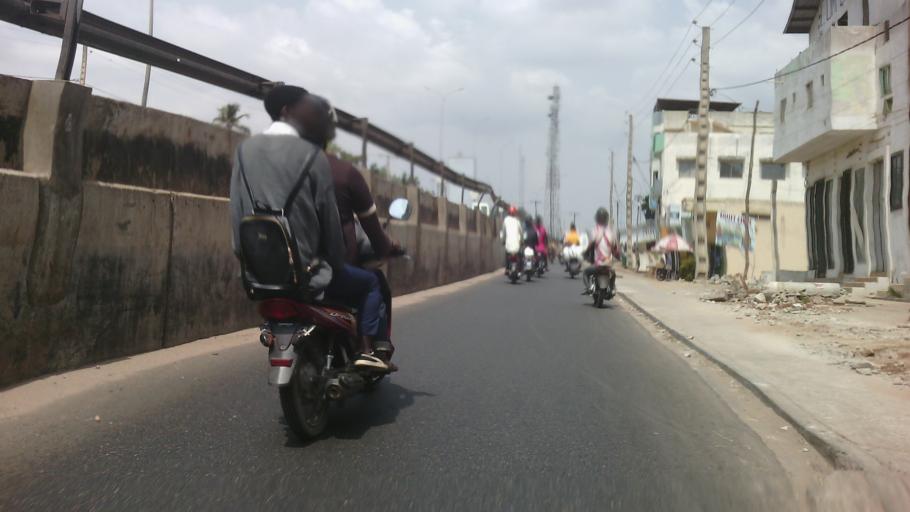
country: BJ
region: Atlantique
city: Abomey-Calavi
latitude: 6.4439
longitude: 2.3540
